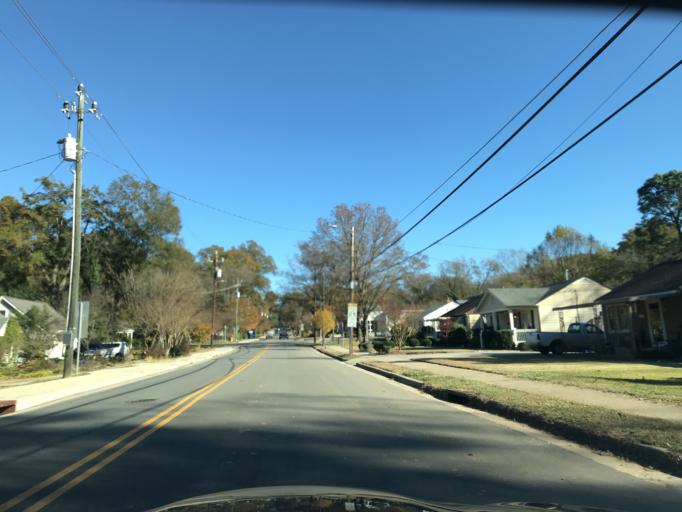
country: US
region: North Carolina
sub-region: Wake County
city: Raleigh
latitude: 35.7930
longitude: -78.6259
